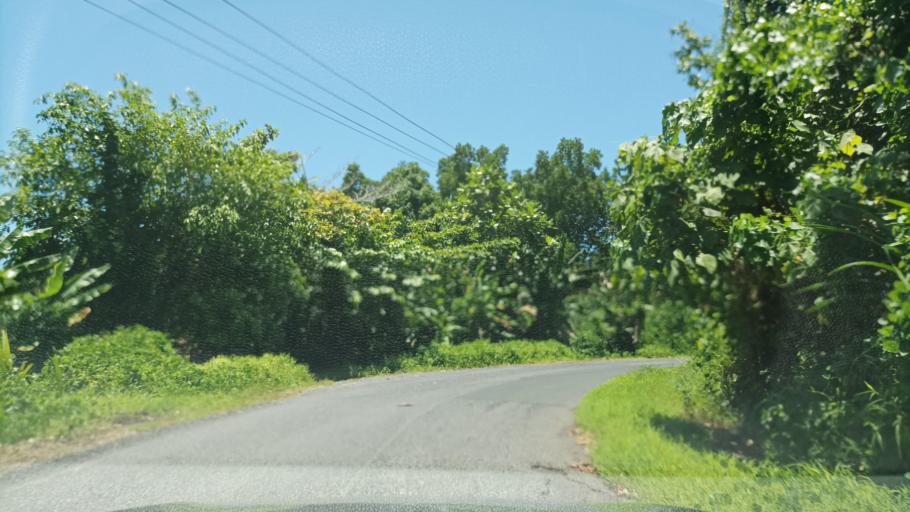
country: FM
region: Pohnpei
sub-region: Madolenihm Municipality
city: Madolenihm Municipality Government
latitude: 6.9212
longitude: 158.3218
